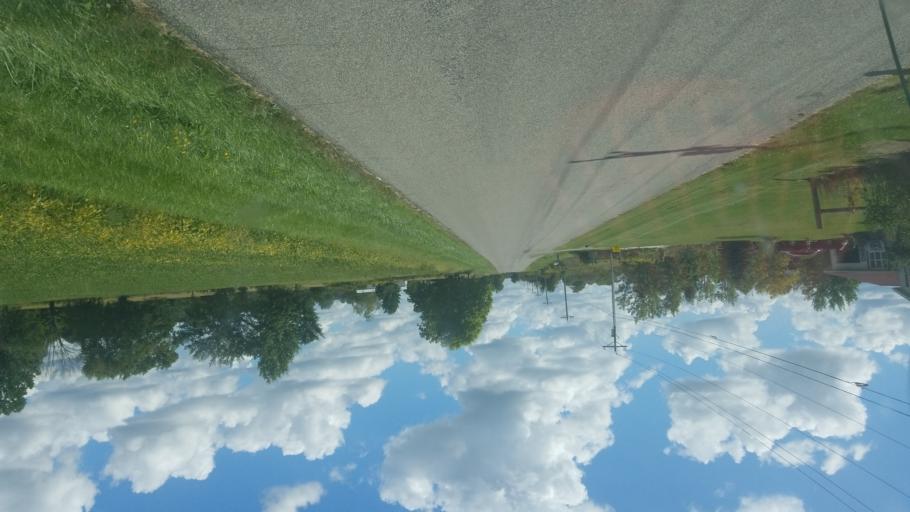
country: US
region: Ohio
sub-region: Champaign County
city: North Lewisburg
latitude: 40.3298
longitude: -83.4963
